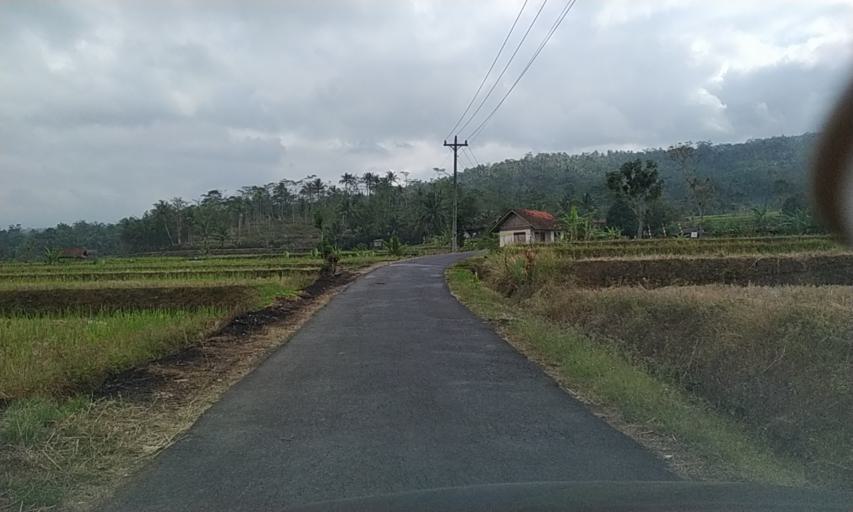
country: ID
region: Central Java
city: Dayeuhluhur
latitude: -7.2535
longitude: 108.6118
